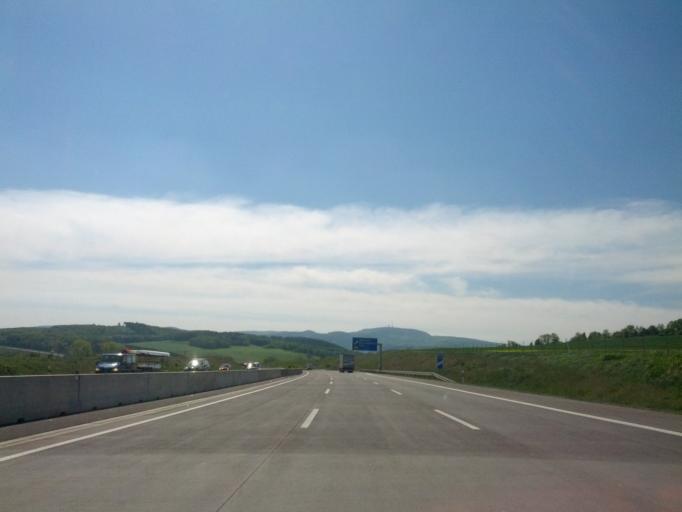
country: DE
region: Thuringia
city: Mechterstadt
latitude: 50.9535
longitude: 10.4858
